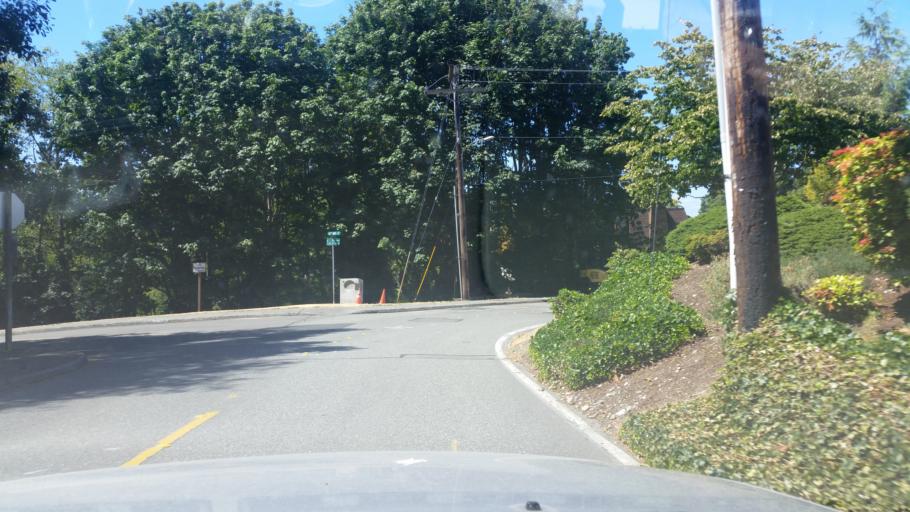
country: US
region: Washington
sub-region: Snohomish County
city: Woodway
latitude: 47.7997
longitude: -122.3743
